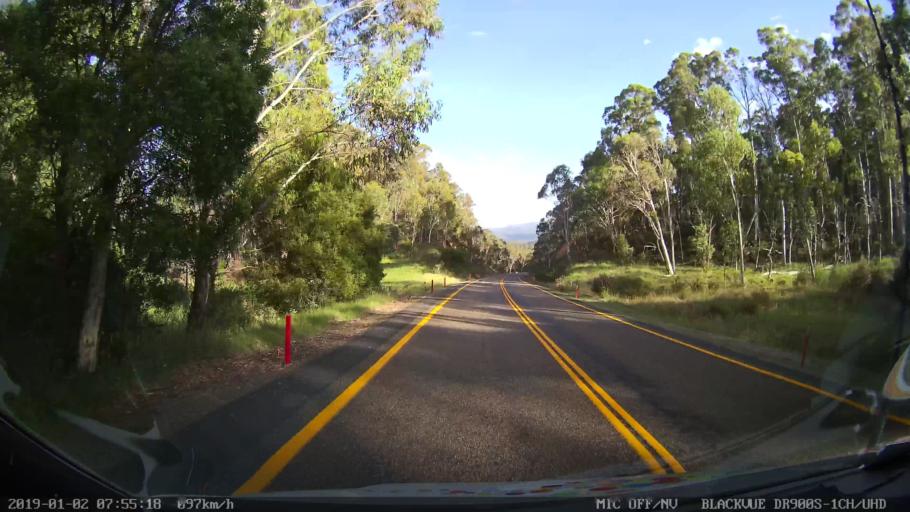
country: AU
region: New South Wales
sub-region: Tumut Shire
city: Tumut
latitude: -35.6869
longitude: 148.4878
